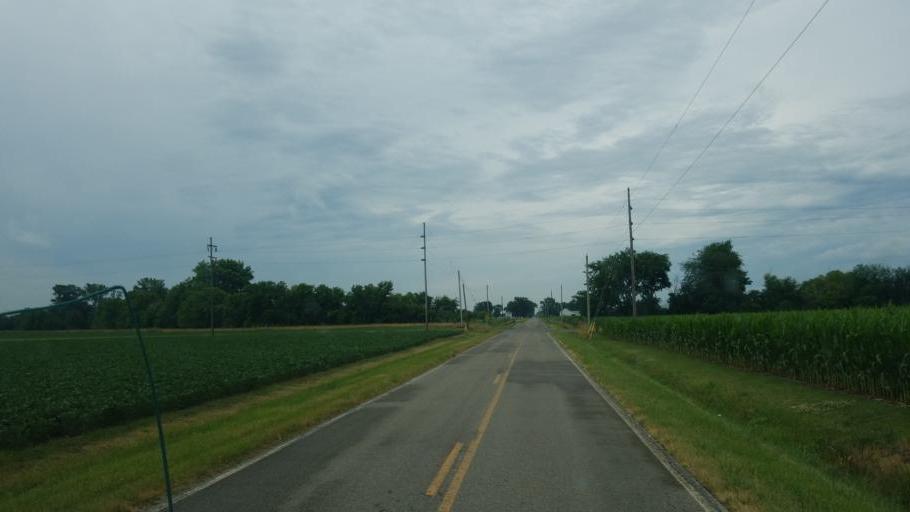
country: US
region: Ohio
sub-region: Defiance County
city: Hicksville
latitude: 41.2824
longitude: -84.6895
